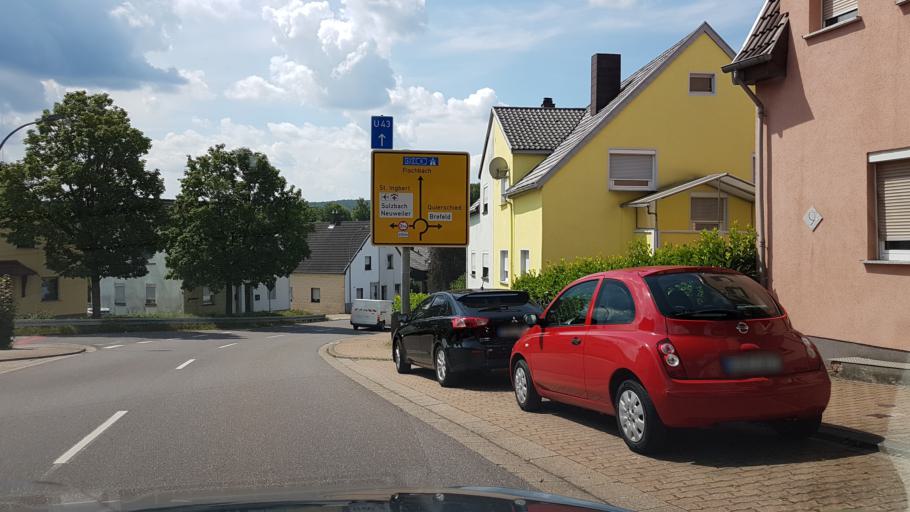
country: DE
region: Saarland
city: Sulzbach
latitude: 49.3074
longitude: 7.0570
